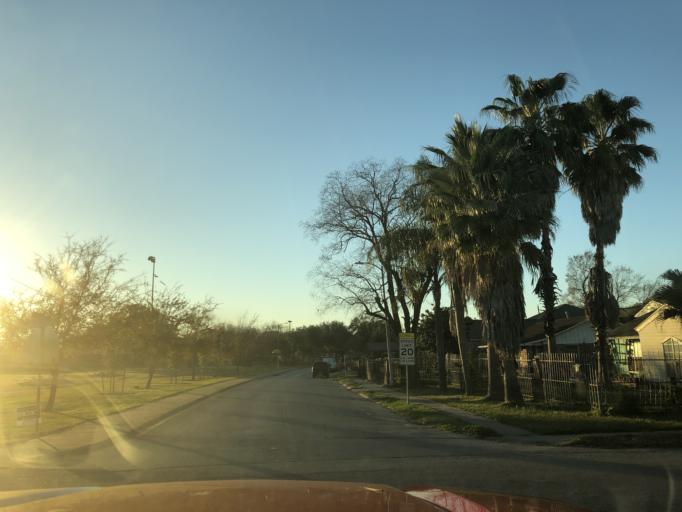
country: US
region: Texas
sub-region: Harris County
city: Jacinto City
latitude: 29.7648
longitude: -95.2700
